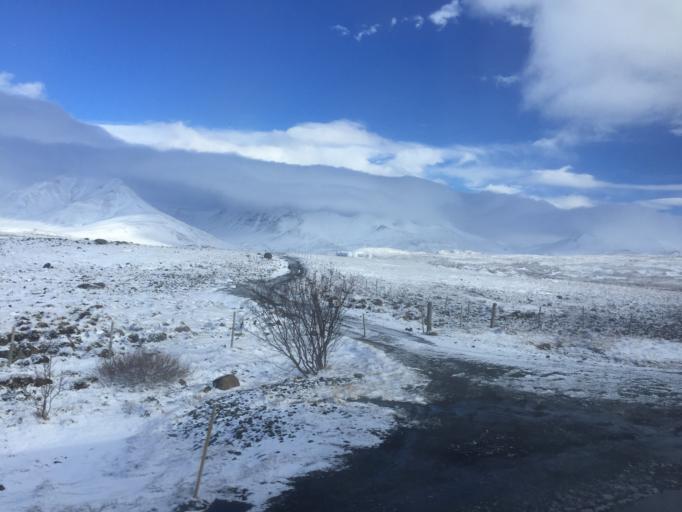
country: IS
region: Capital Region
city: Mosfellsbaer
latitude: 64.1826
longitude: -21.5728
